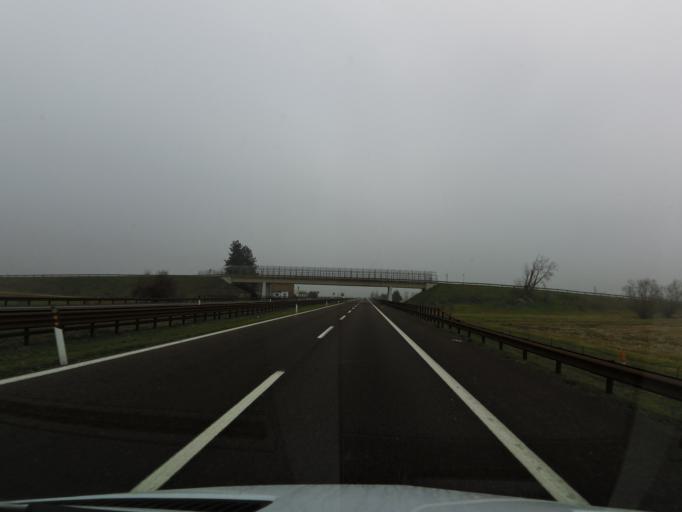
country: IT
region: Emilia-Romagna
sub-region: Provincia di Modena
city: Migliarina
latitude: 44.8362
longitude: 10.8526
